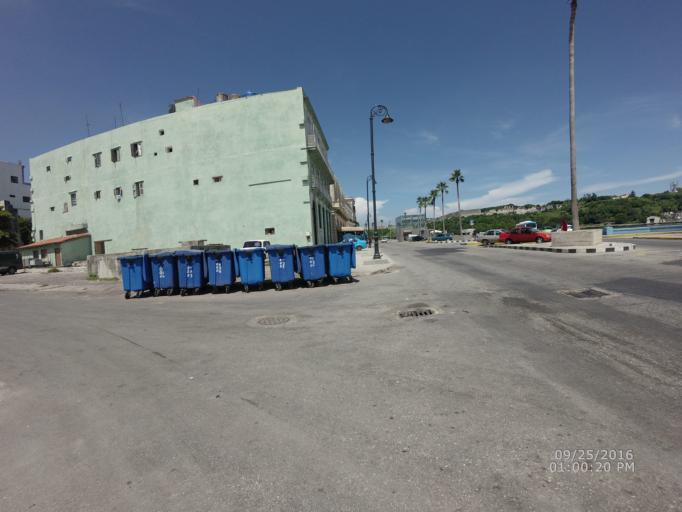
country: CU
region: La Habana
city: La Habana Vieja
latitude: 23.1397
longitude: -82.3481
